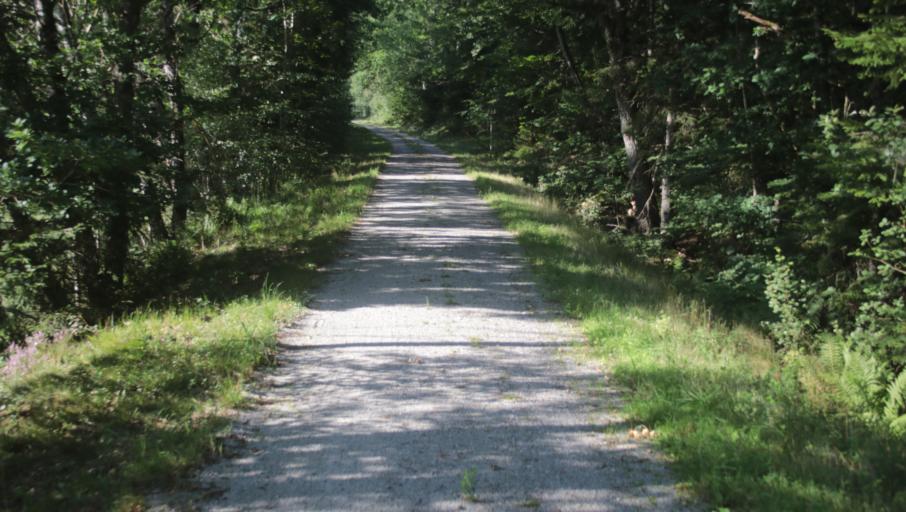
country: SE
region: Blekinge
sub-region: Karlshamns Kommun
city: Svangsta
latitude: 56.3318
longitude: 14.6996
